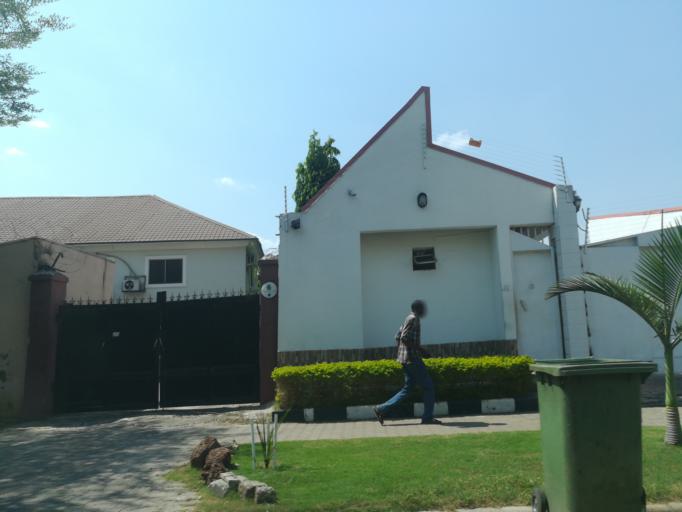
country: NG
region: Abuja Federal Capital Territory
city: Abuja
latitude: 9.0637
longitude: 7.4215
